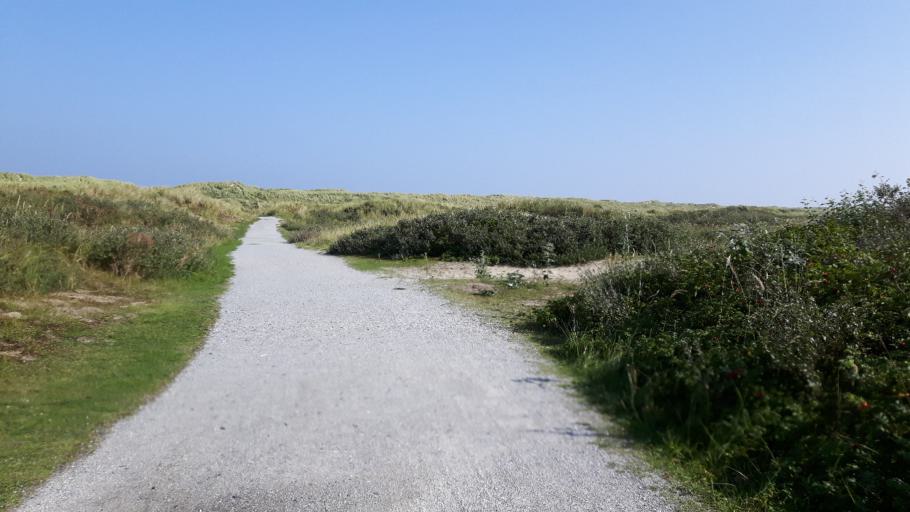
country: NL
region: Friesland
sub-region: Gemeente Ameland
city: Nes
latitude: 53.4597
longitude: 5.8162
